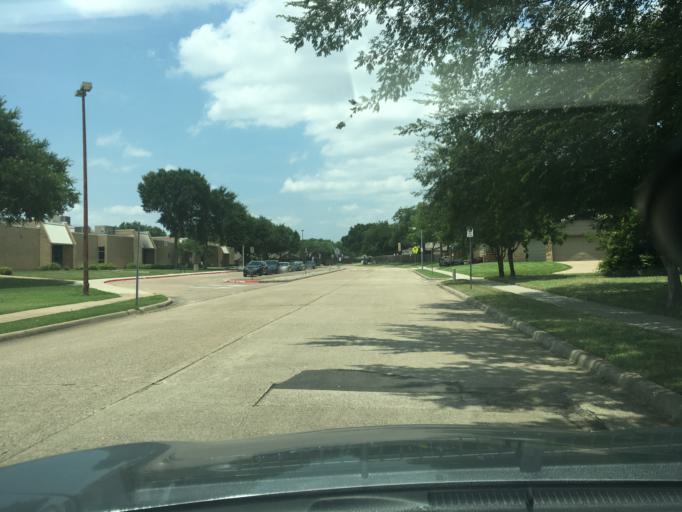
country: US
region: Texas
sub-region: Dallas County
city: Richardson
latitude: 32.9531
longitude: -96.6885
